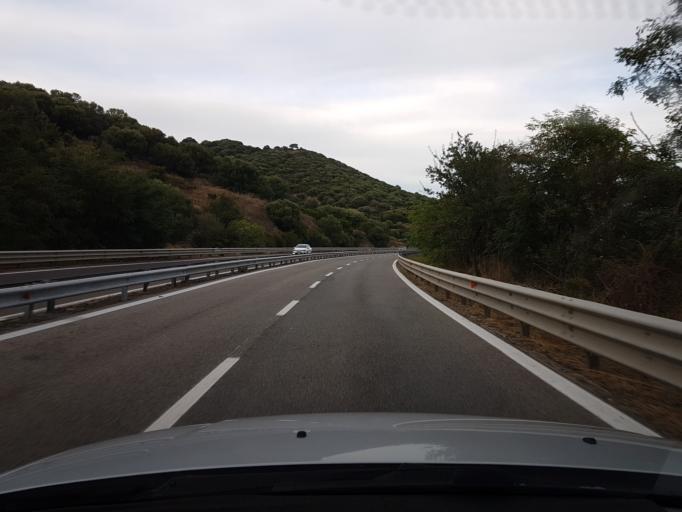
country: IT
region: Sardinia
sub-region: Provincia di Nuoro
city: Nuoro
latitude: 40.3552
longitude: 9.3454
